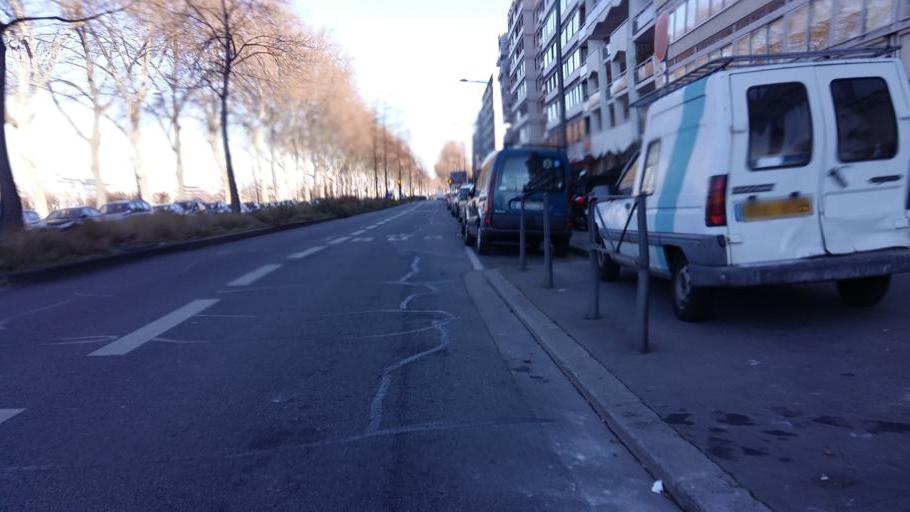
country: FR
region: Rhone-Alpes
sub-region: Departement du Rhone
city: La Mulatiere
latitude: 45.7374
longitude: 4.8246
